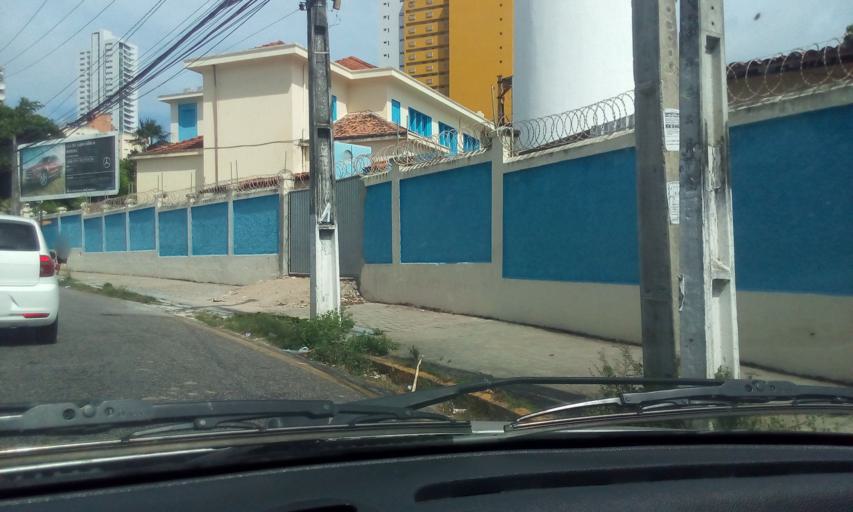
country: BR
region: Rio Grande do Norte
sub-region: Natal
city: Natal
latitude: -5.7905
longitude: -35.2056
